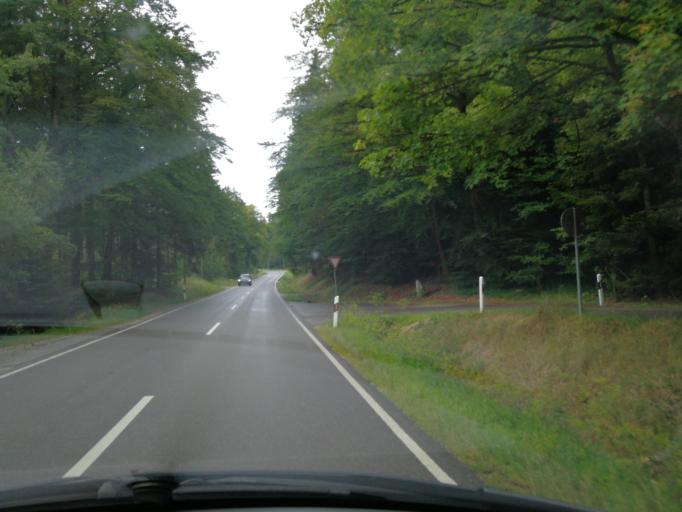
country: DE
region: Bavaria
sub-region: Upper Palatinate
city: Wiesent
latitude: 49.0351
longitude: 12.3720
